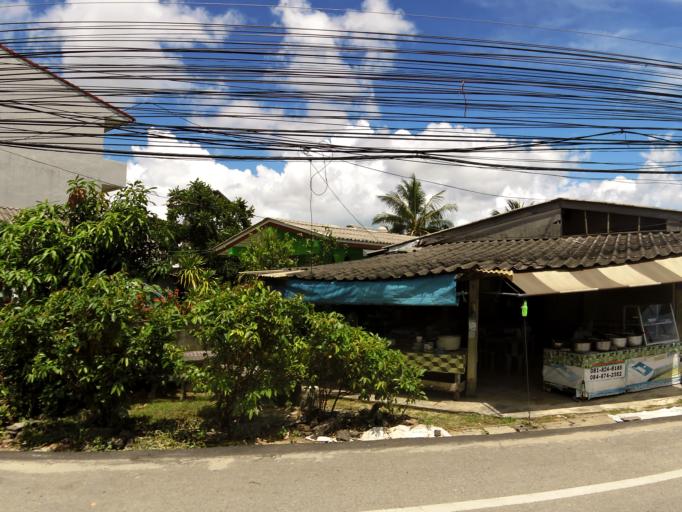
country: TH
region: Phuket
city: Ban Chalong
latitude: 7.8332
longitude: 98.3386
